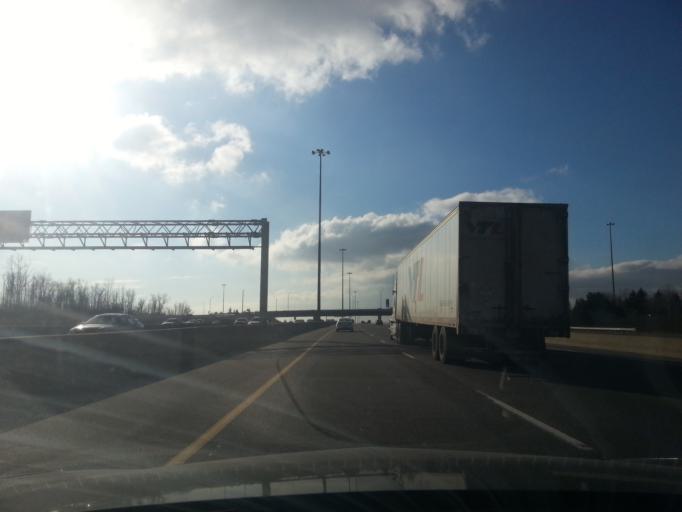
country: CA
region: Ontario
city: Pickering
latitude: 43.8188
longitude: -79.1115
